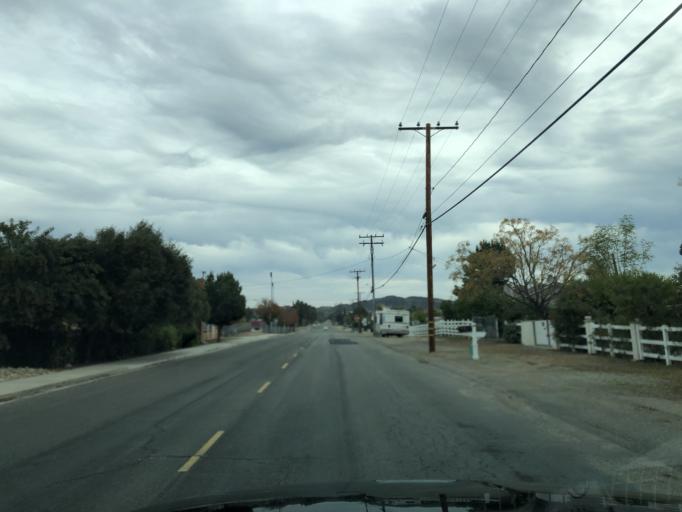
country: US
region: California
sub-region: Riverside County
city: Sedco Hills
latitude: 33.6232
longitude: -117.2855
